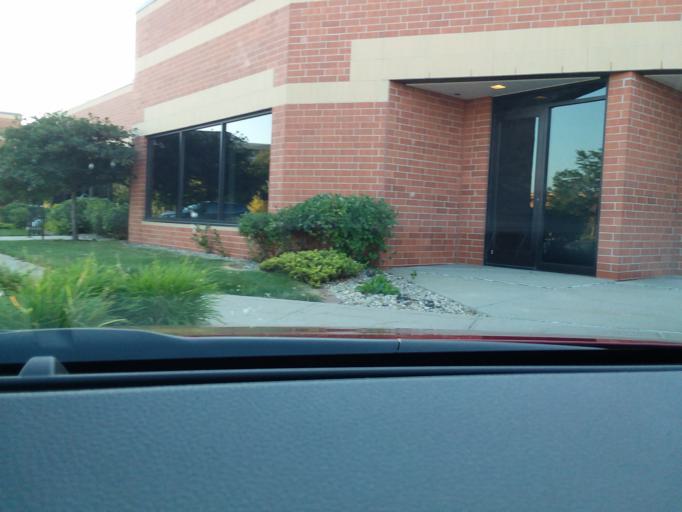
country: US
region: Wisconsin
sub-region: Dane County
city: Windsor
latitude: 43.1457
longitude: -89.2939
